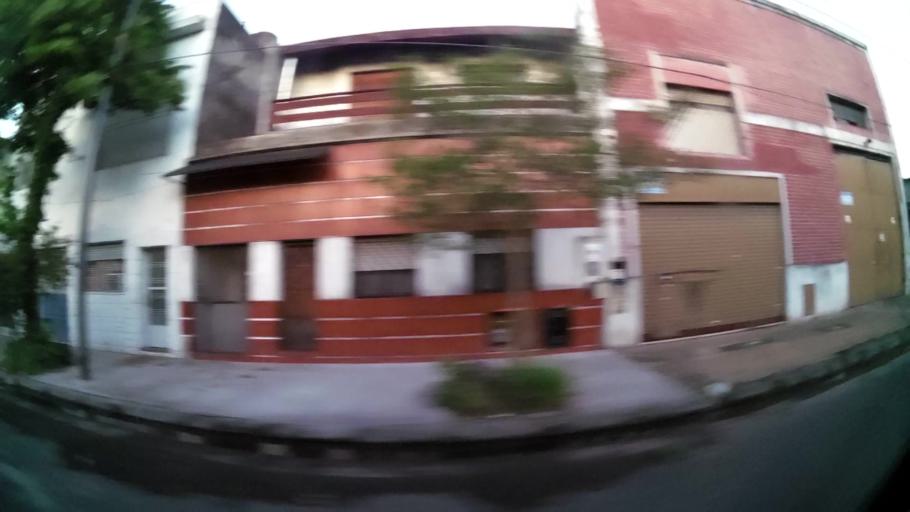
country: AR
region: Buenos Aires F.D.
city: Villa Lugano
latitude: -34.6438
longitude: -58.4341
